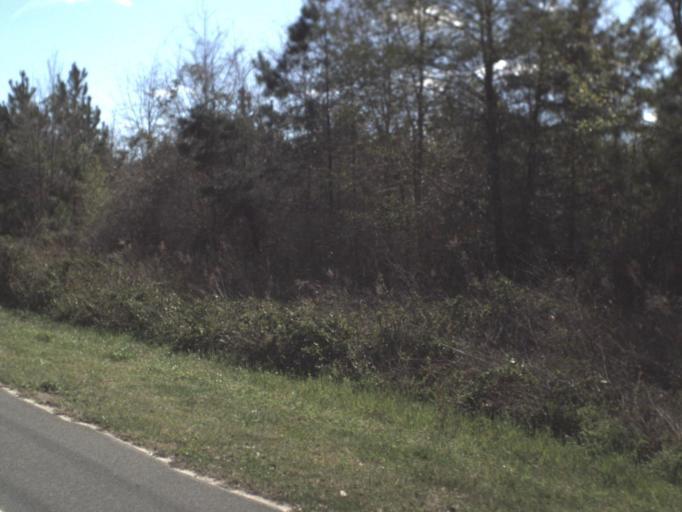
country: US
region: Florida
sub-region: Gadsden County
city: Gretna
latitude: 30.6000
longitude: -84.6511
